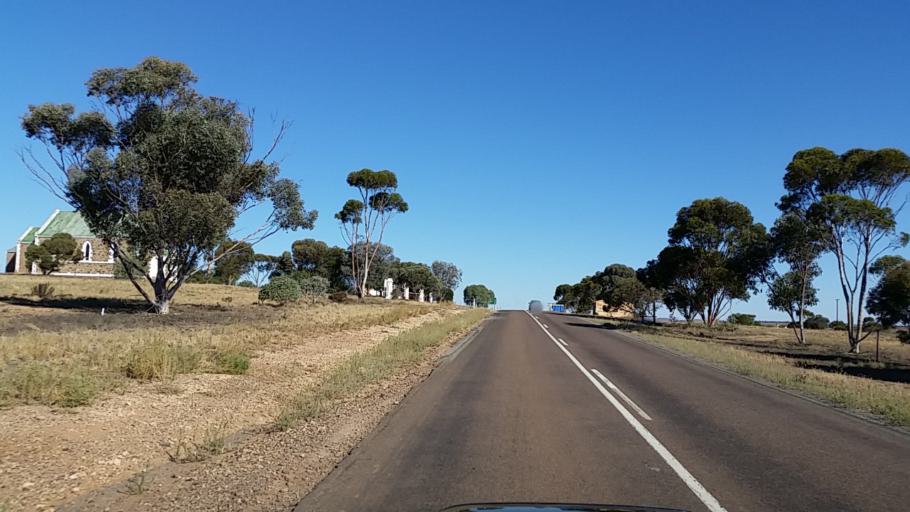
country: AU
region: South Australia
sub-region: Flinders Ranges
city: Quorn
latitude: -32.4262
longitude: 138.5309
